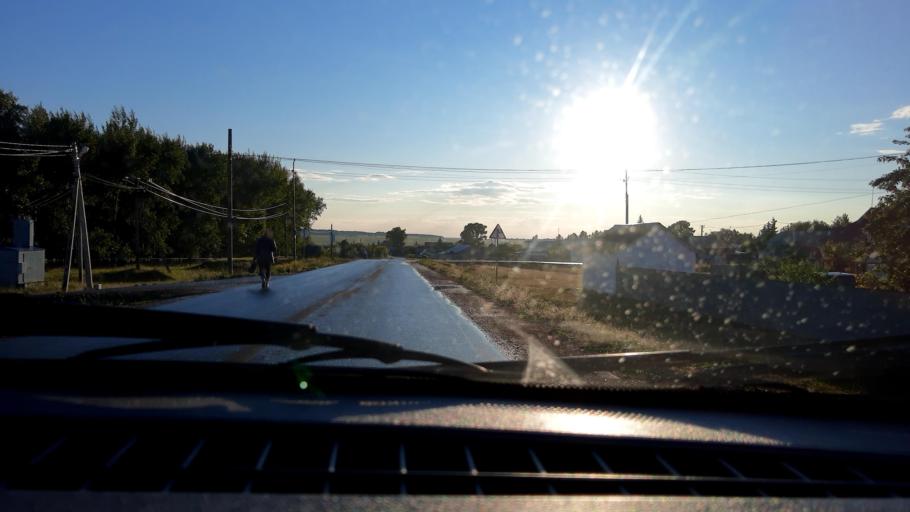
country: RU
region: Bashkortostan
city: Avdon
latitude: 54.8154
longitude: 55.7019
